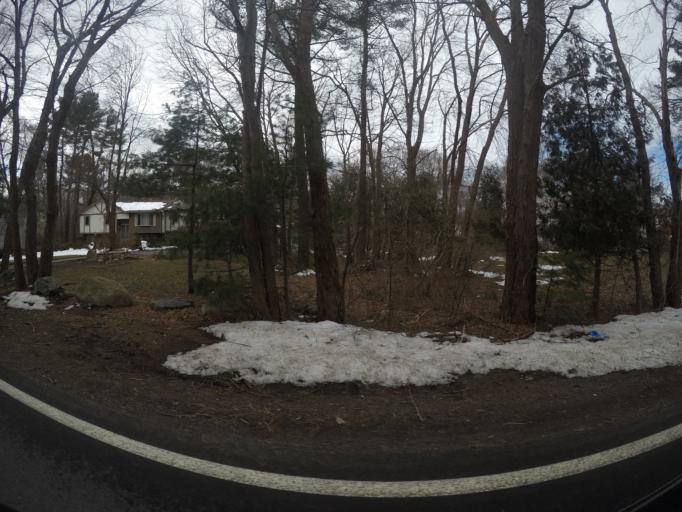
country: US
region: Massachusetts
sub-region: Bristol County
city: Easton
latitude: 42.0499
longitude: -71.1287
